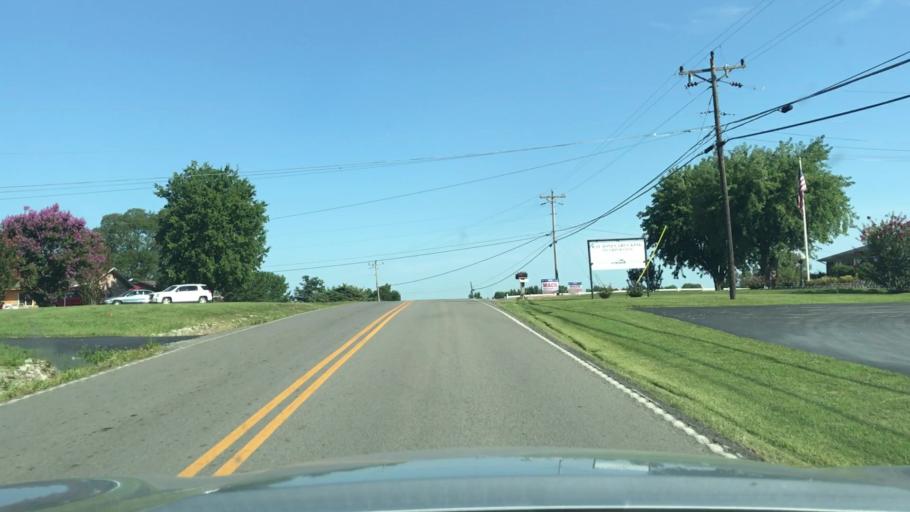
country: US
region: Kentucky
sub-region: Muhlenberg County
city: Greenville
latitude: 37.1648
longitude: -87.1451
